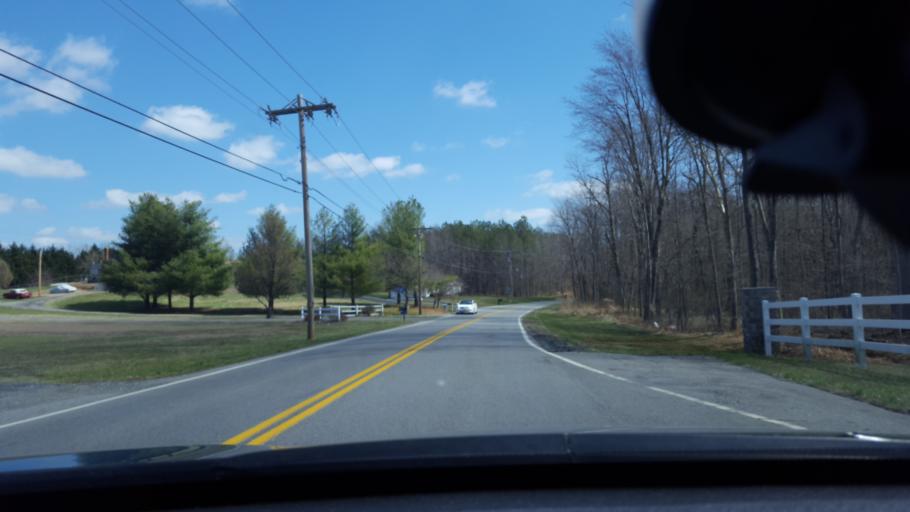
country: US
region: Maryland
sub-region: Calvert County
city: Huntingtown
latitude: 38.6284
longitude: -76.5890
